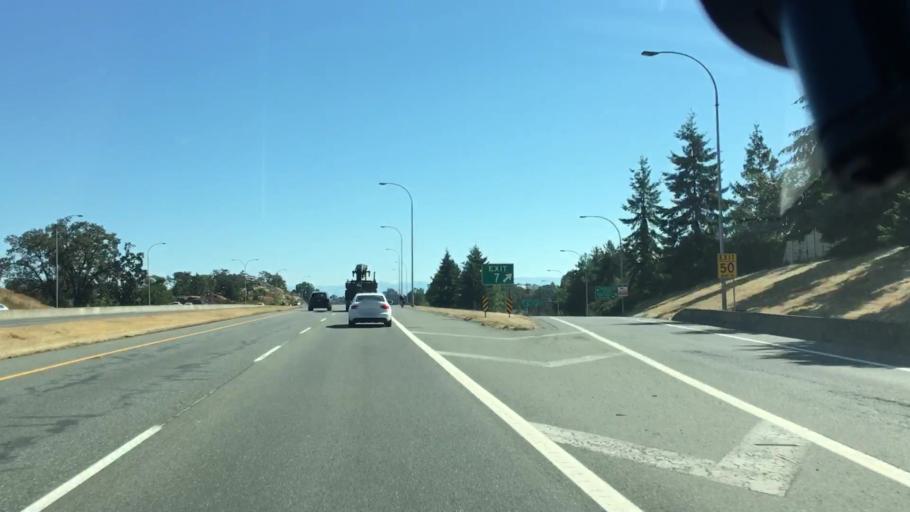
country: CA
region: British Columbia
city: Victoria
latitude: 48.4712
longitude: -123.3827
